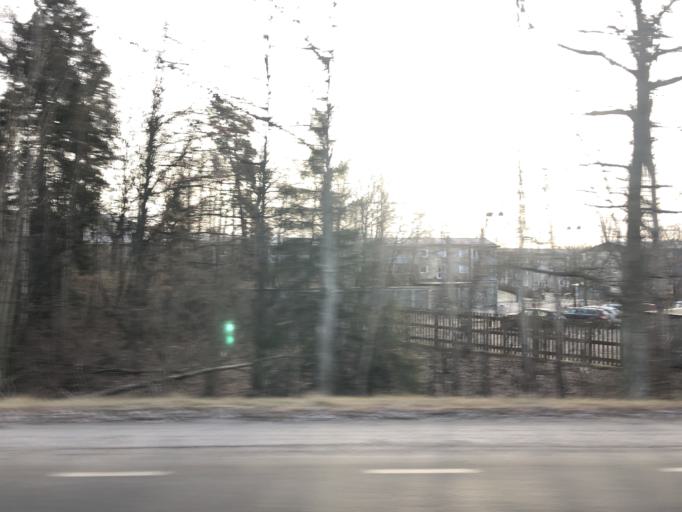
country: SE
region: Stockholm
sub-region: Jarfalla Kommun
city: Jakobsberg
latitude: 59.4152
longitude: 17.7990
